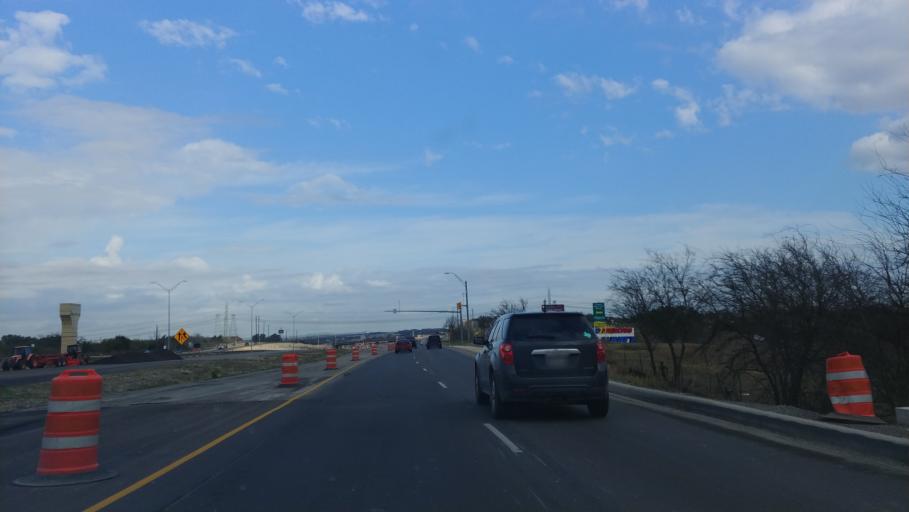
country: US
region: Texas
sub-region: Bexar County
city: Lackland Air Force Base
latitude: 29.4099
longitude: -98.7092
